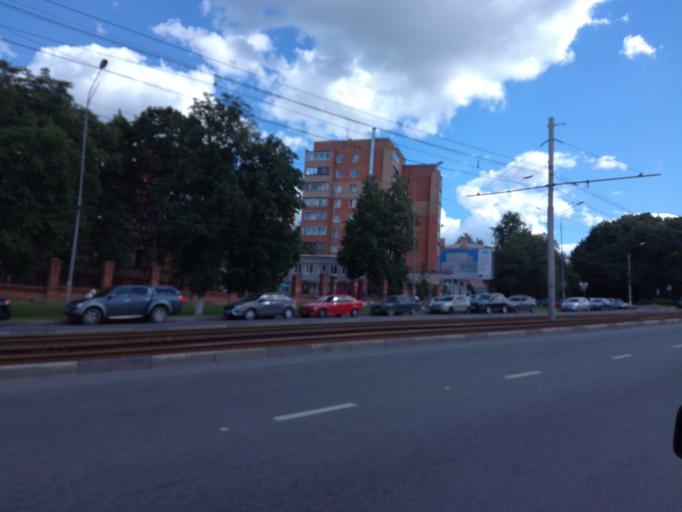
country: RU
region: Kursk
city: Kursk
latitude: 51.7518
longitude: 36.2001
